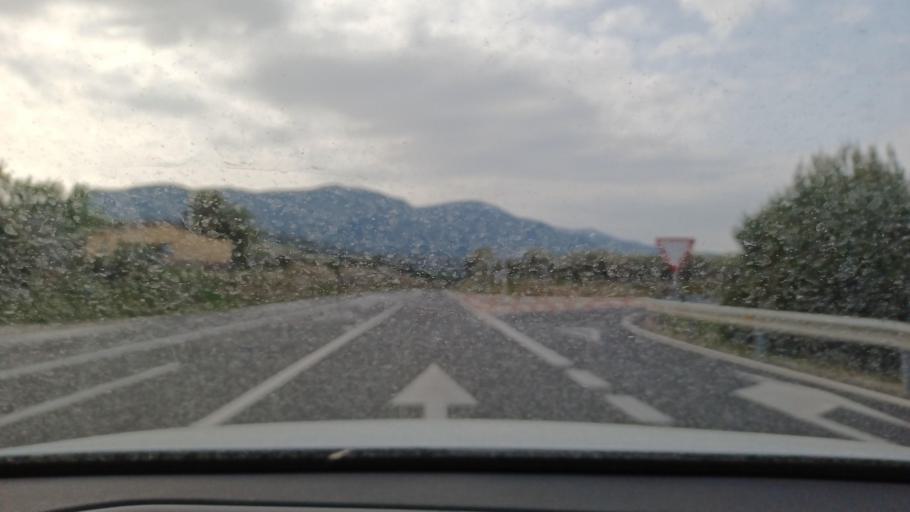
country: ES
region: Catalonia
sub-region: Provincia de Tarragona
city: Masdenverge
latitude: 40.6771
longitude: 0.5260
